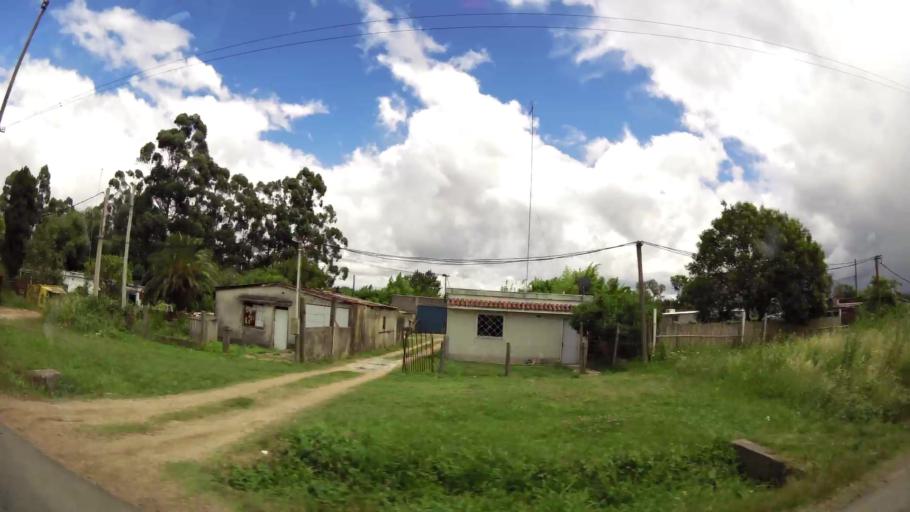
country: UY
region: Canelones
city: La Paz
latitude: -34.8157
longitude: -56.1682
